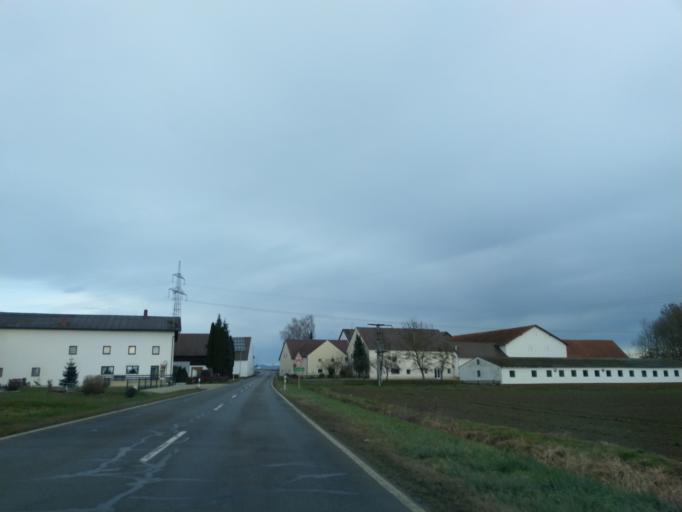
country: DE
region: Bavaria
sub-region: Lower Bavaria
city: Osterhofen
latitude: 48.6743
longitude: 12.9940
